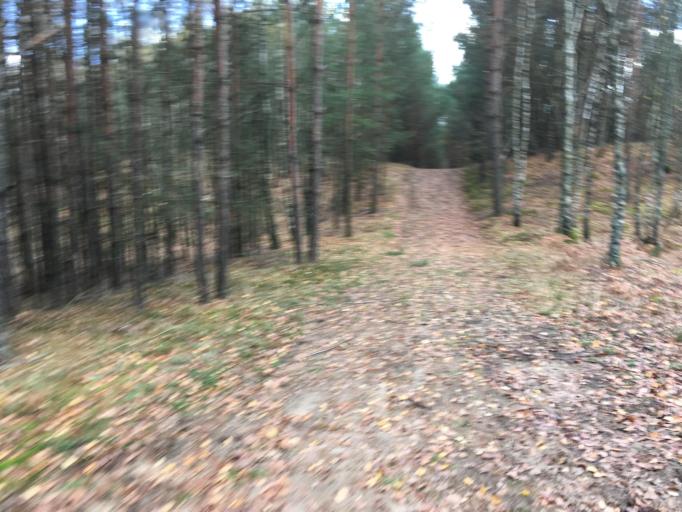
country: DE
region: Brandenburg
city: Birkenwerder
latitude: 52.7031
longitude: 13.3376
